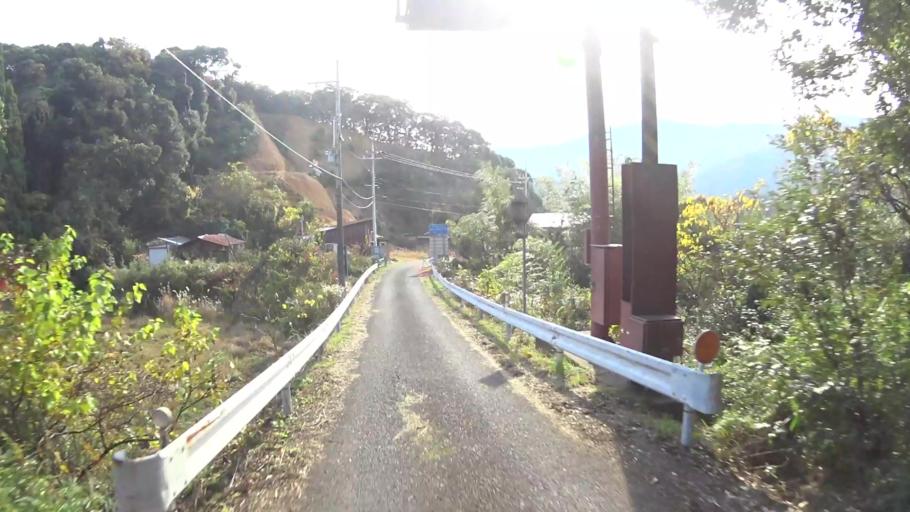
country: JP
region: Kyoto
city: Maizuru
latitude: 35.5602
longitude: 135.4041
